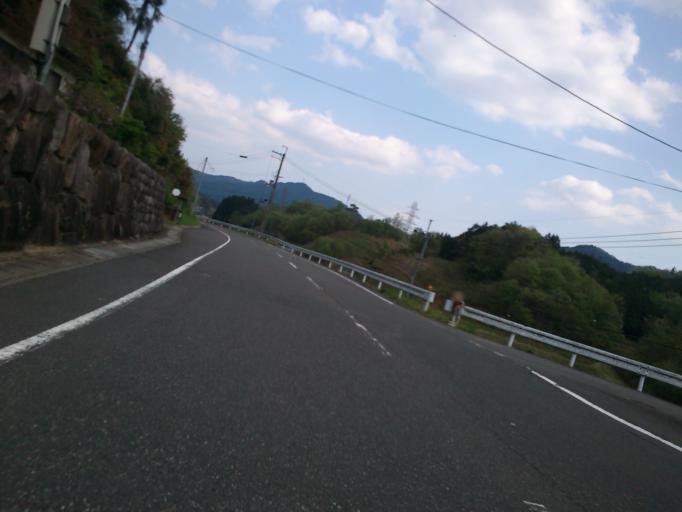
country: JP
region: Kyoto
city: Fukuchiyama
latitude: 35.3184
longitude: 134.9578
